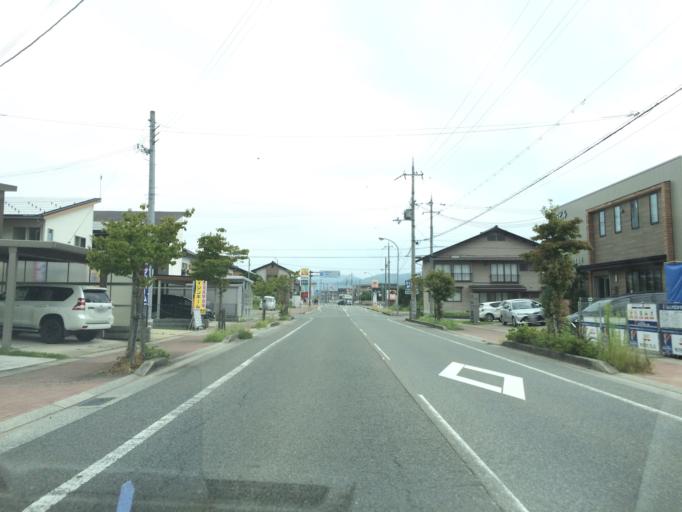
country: JP
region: Hyogo
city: Toyooka
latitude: 35.5399
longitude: 134.8094
